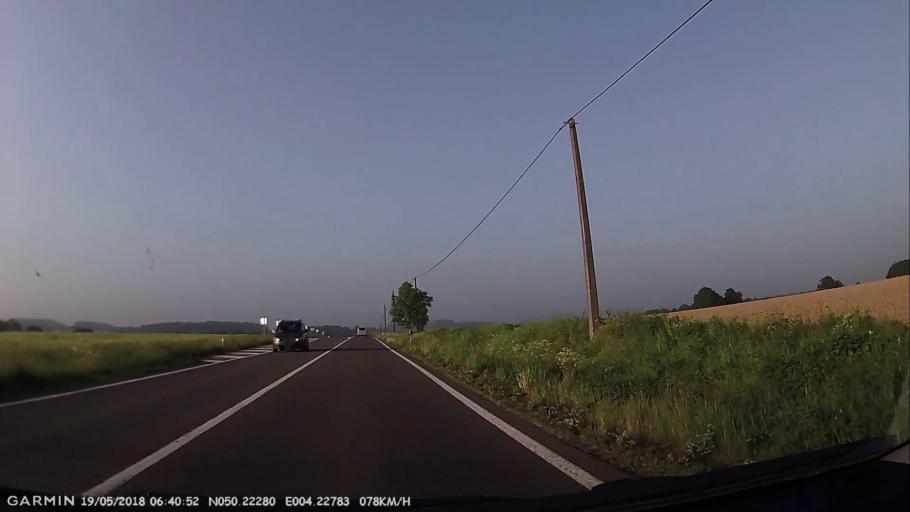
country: BE
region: Wallonia
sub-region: Province du Hainaut
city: Beaumont
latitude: 50.2227
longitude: 4.2278
